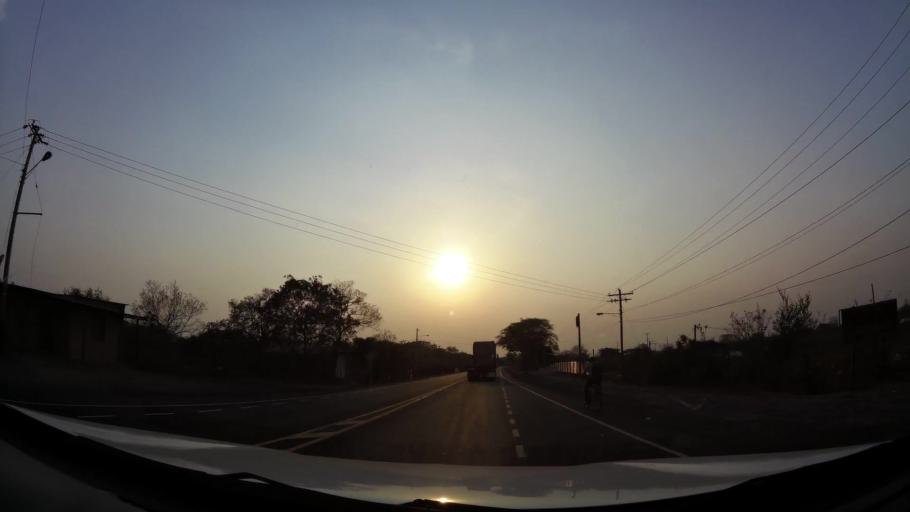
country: NI
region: Leon
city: Nagarote
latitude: 12.2741
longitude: -86.5694
